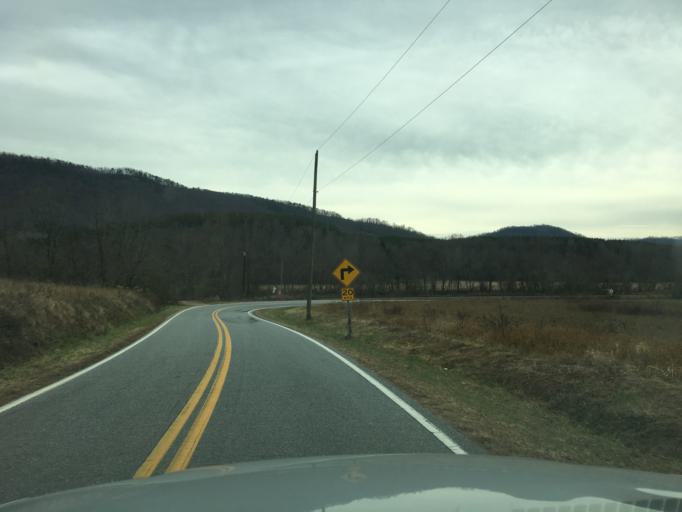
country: US
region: North Carolina
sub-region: McDowell County
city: West Marion
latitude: 35.6247
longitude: -81.9669
